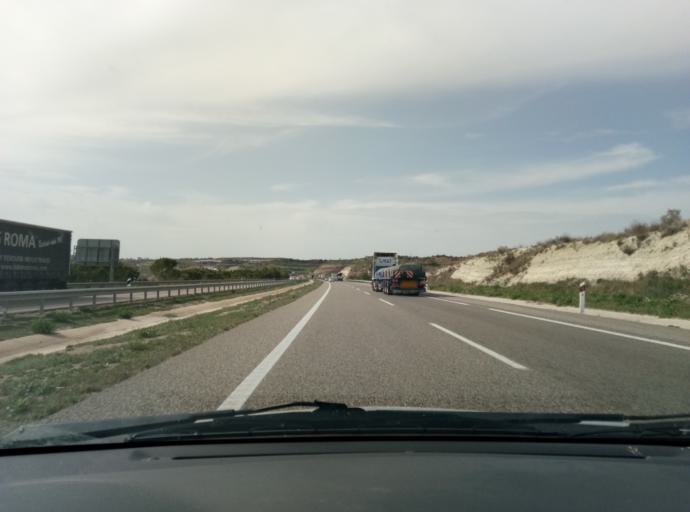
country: ES
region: Catalonia
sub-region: Provincia de Lleida
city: Cervera
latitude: 41.6587
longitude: 1.3102
